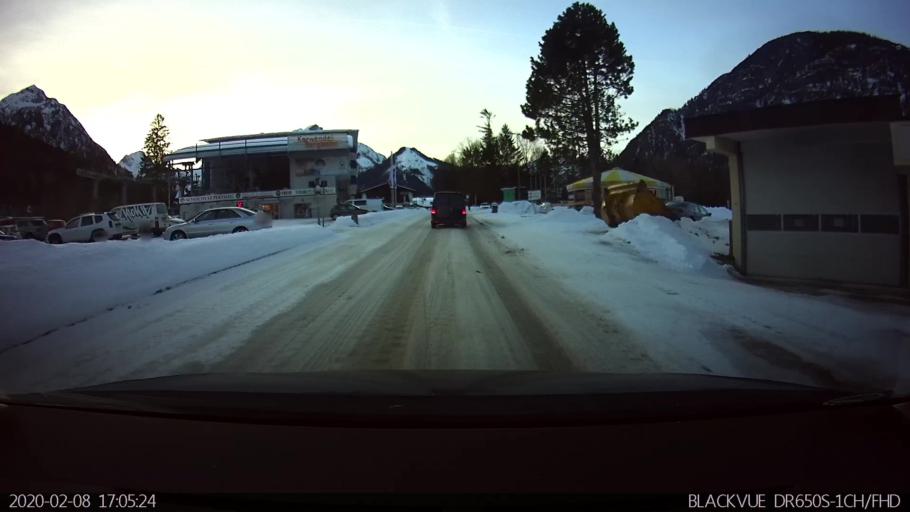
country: AT
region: Tyrol
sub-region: Politischer Bezirk Schwaz
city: Stans
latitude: 47.4372
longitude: 11.6978
